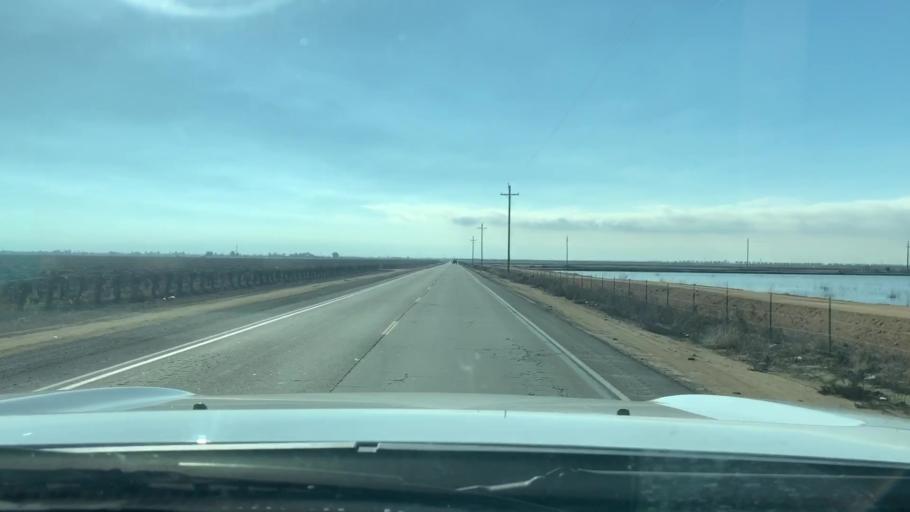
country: US
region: California
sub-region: Kern County
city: Rosedale
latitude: 35.4650
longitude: -119.1536
